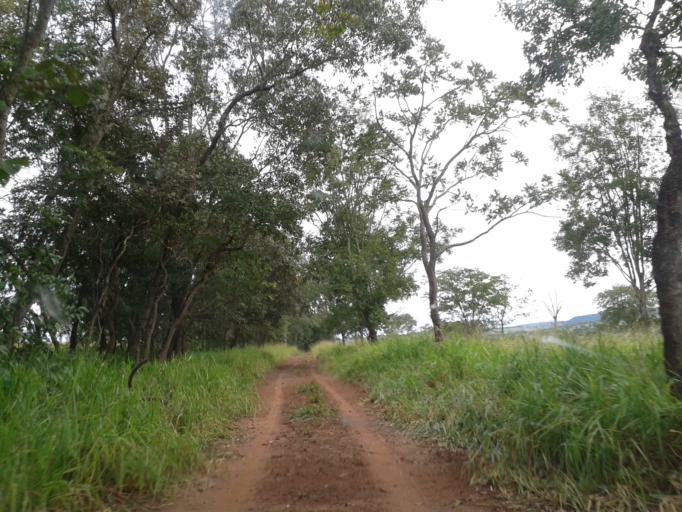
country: BR
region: Minas Gerais
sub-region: Campina Verde
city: Campina Verde
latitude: -19.4867
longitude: -49.6241
